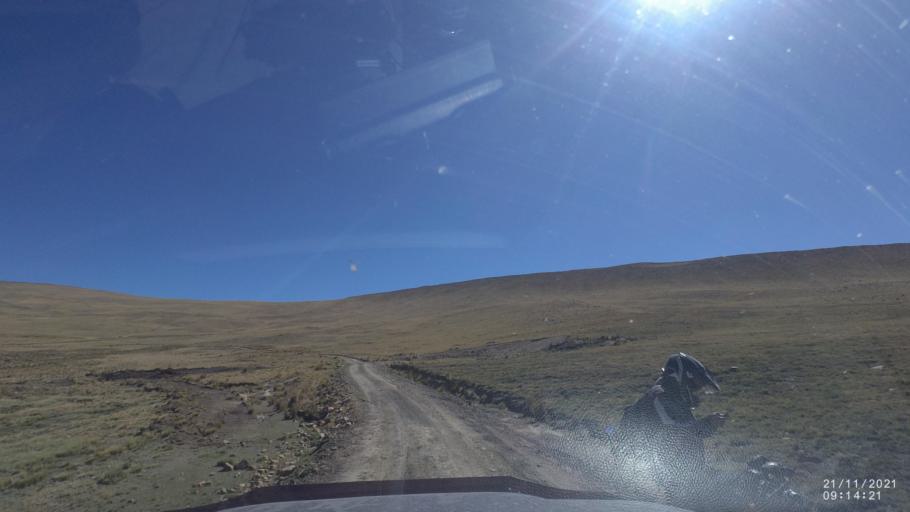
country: BO
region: Cochabamba
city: Cochabamba
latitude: -17.1356
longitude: -66.2574
